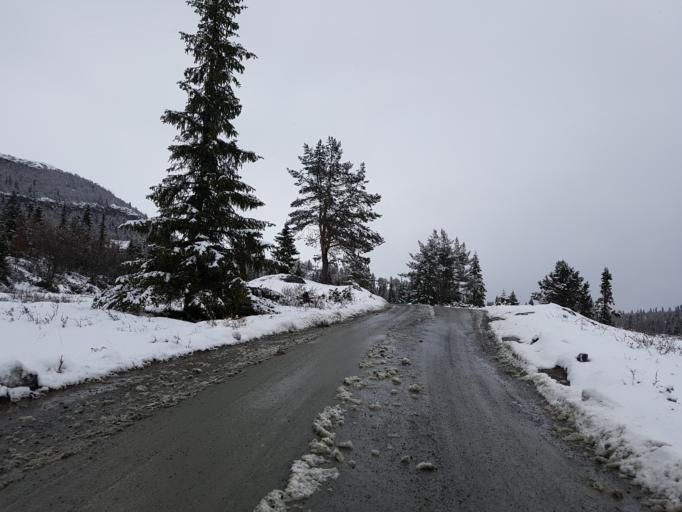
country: NO
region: Oppland
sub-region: Sel
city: Otta
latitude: 61.8049
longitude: 9.6939
